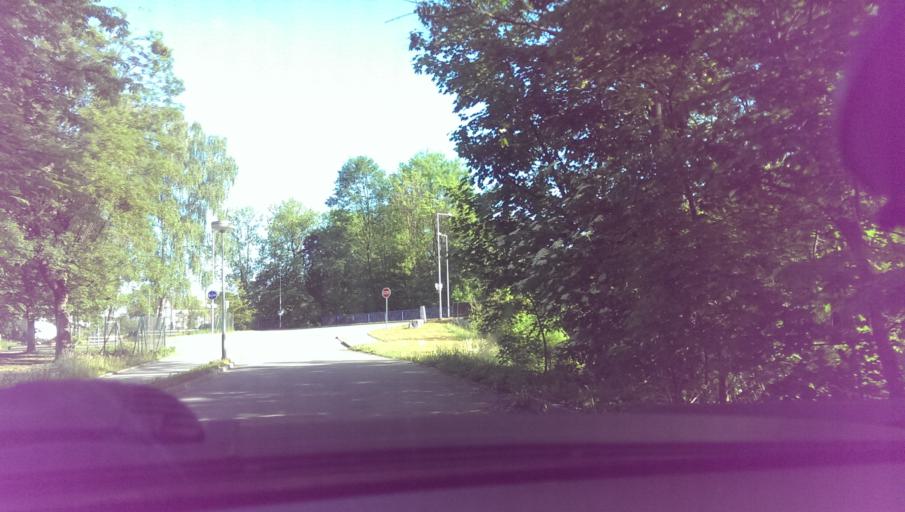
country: CZ
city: Frydlant nad Ostravici
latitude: 49.5834
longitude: 18.3649
